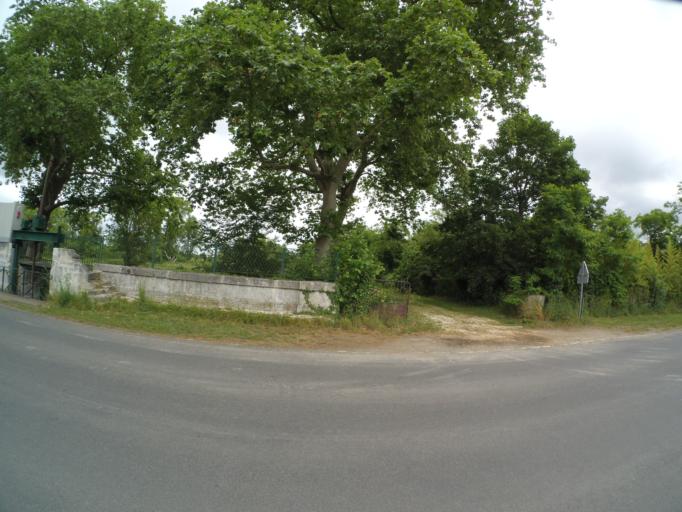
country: FR
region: Poitou-Charentes
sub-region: Departement de la Charente-Maritime
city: Saint-Laurent-de-la-Pree
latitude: 45.9819
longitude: -1.0019
